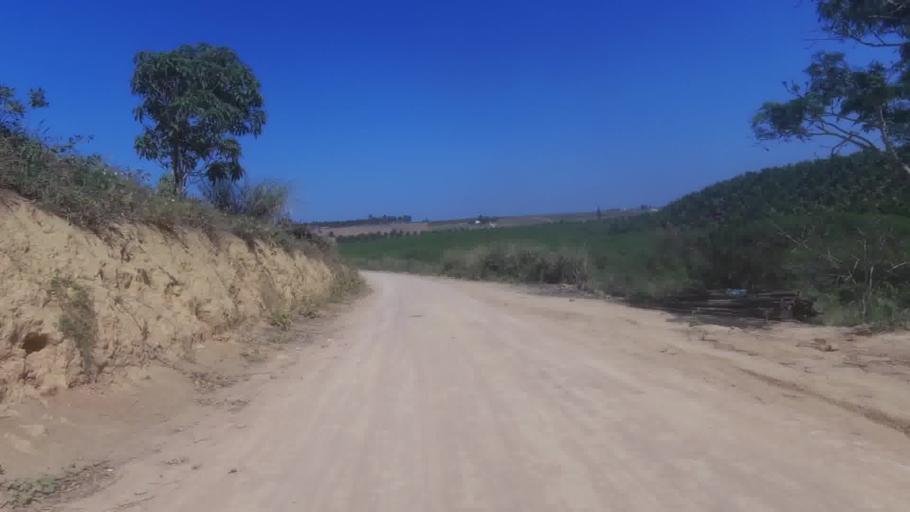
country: BR
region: Espirito Santo
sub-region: Marataizes
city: Marataizes
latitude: -21.1033
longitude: -40.8531
